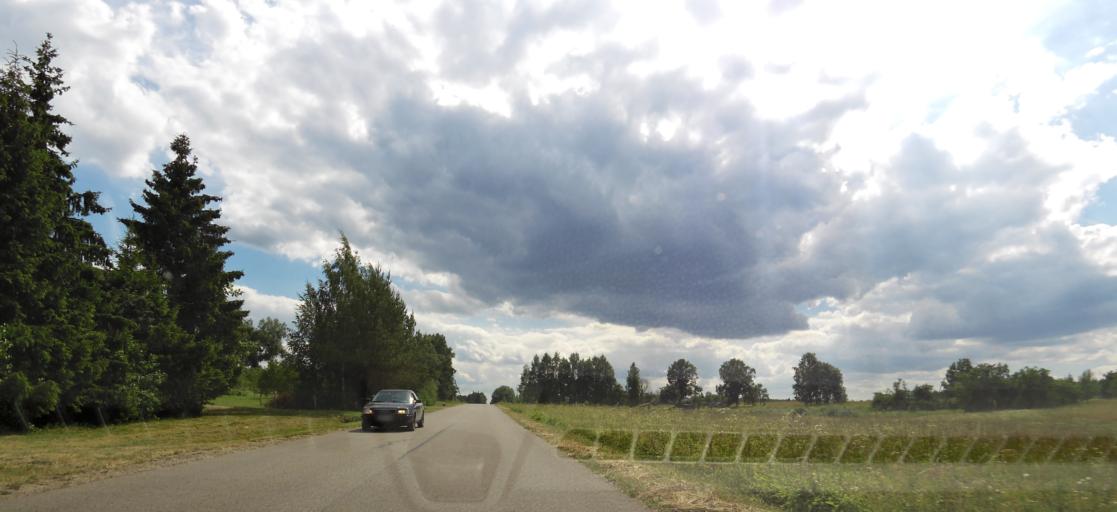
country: LT
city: Skaidiskes
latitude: 54.5350
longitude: 25.6441
